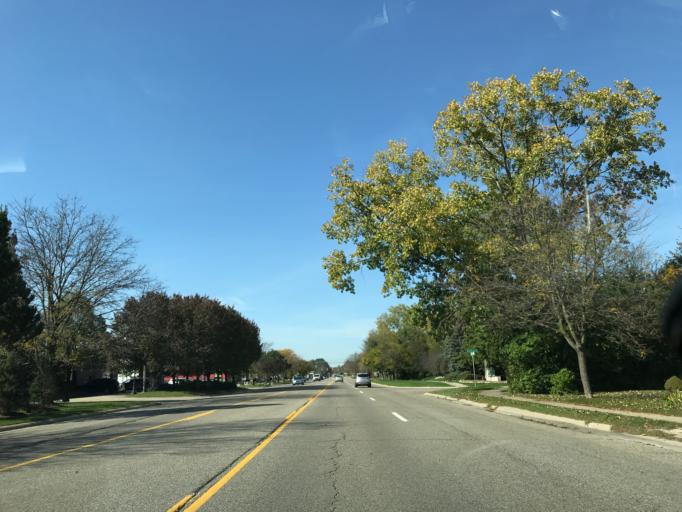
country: US
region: Michigan
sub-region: Oakland County
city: Farmington
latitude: 42.4703
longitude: -83.3515
